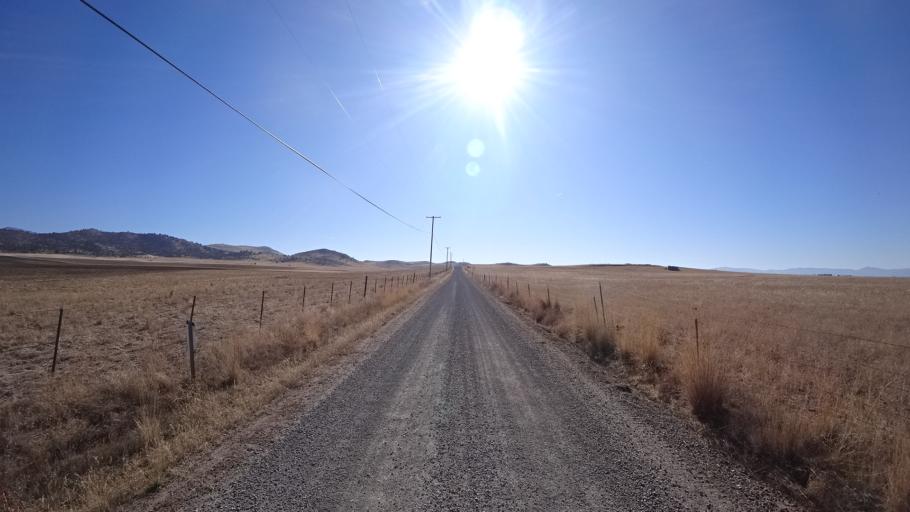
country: US
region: California
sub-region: Siskiyou County
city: Montague
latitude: 41.8035
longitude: -122.4159
